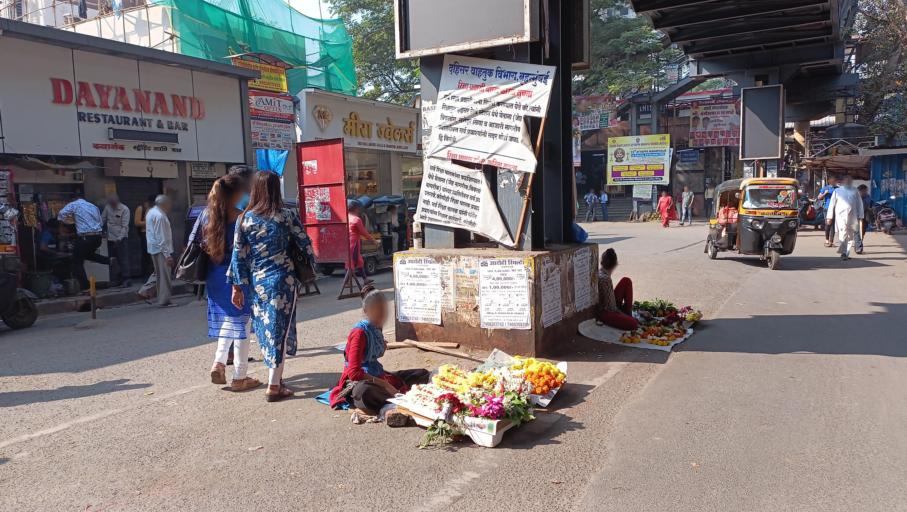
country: IN
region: Maharashtra
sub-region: Mumbai Suburban
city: Borivli
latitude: 19.2496
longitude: 72.8601
